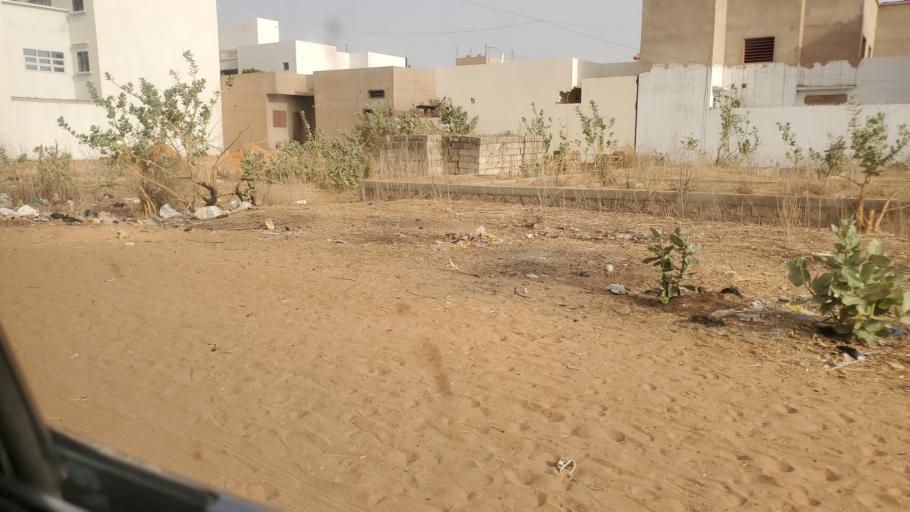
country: SN
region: Louga
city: Louga
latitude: 15.6266
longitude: -16.2404
